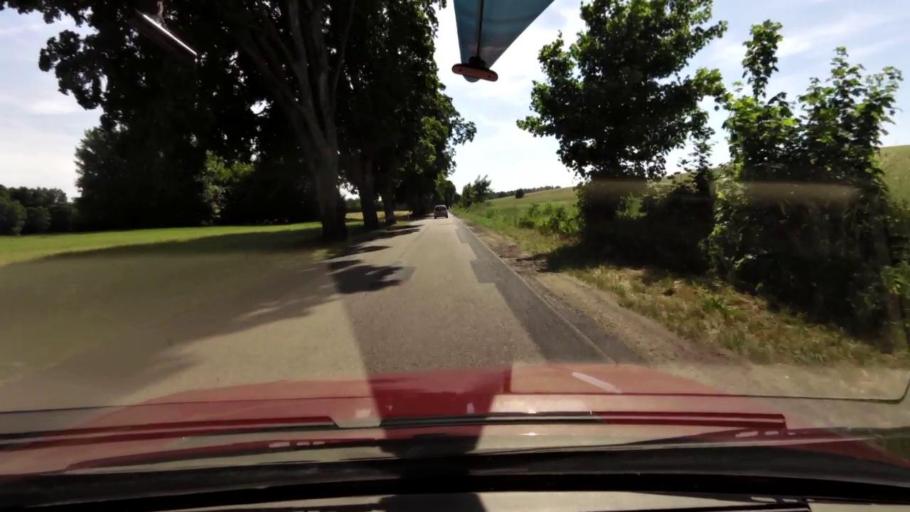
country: PL
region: Pomeranian Voivodeship
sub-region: Powiat slupski
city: Kepice
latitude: 54.2709
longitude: 16.9565
